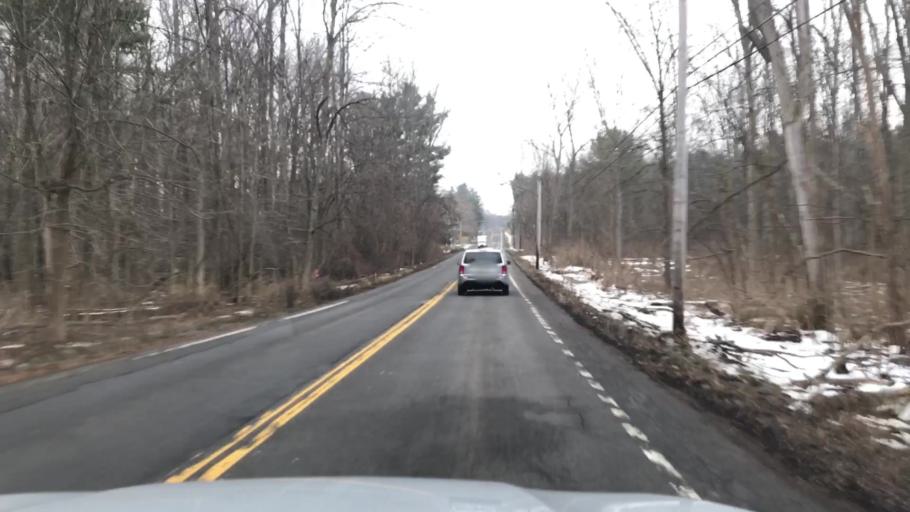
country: US
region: New York
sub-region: Erie County
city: Orchard Park
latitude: 42.7464
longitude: -78.7759
